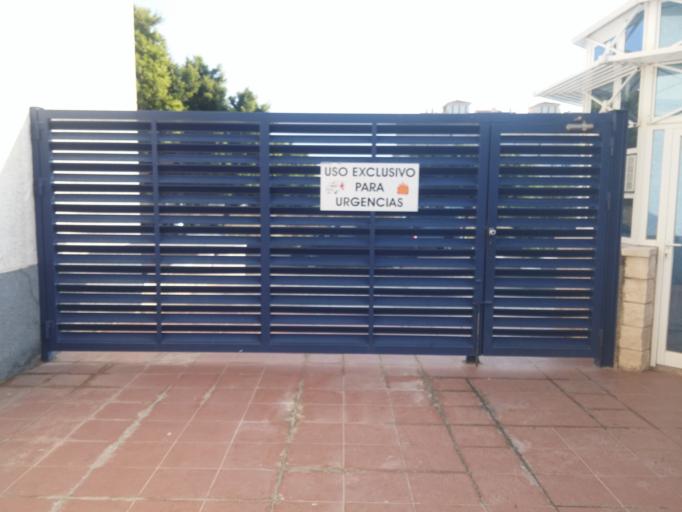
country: ES
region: Valencia
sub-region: Provincia de Alicante
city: Villajoyosa
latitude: 38.5017
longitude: -0.2442
